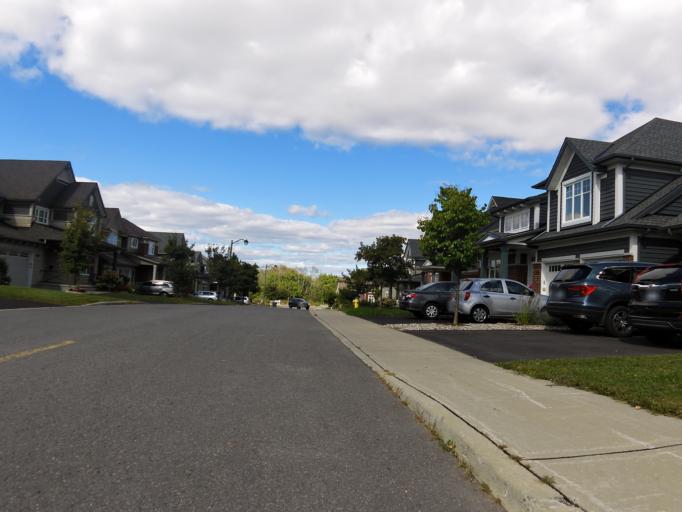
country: CA
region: Ontario
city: Ottawa
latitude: 45.3568
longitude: -75.6396
